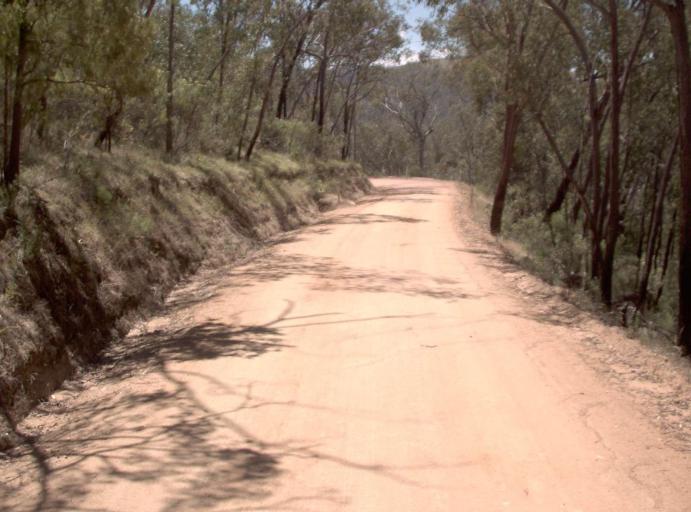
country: AU
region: New South Wales
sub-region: Snowy River
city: Jindabyne
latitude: -36.9666
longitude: 148.3064
